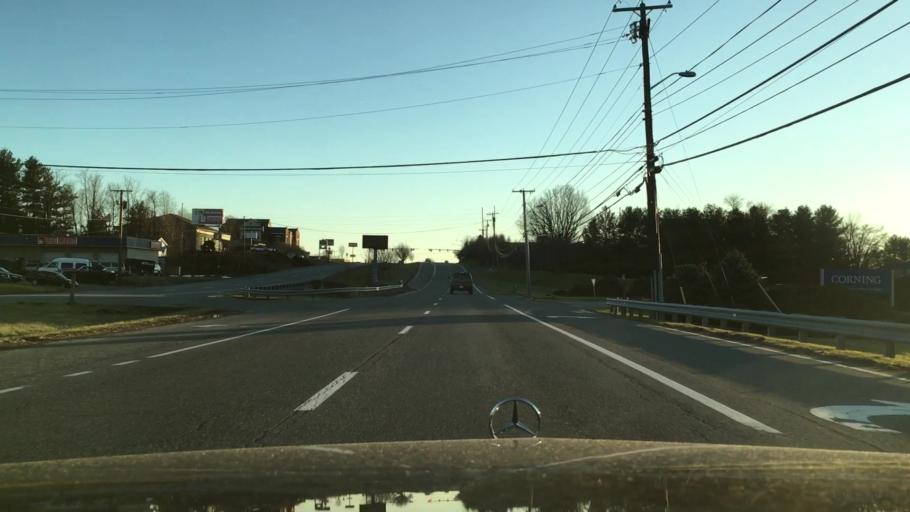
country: US
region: Virginia
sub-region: Montgomery County
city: Merrimac
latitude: 37.1727
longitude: -80.4206
